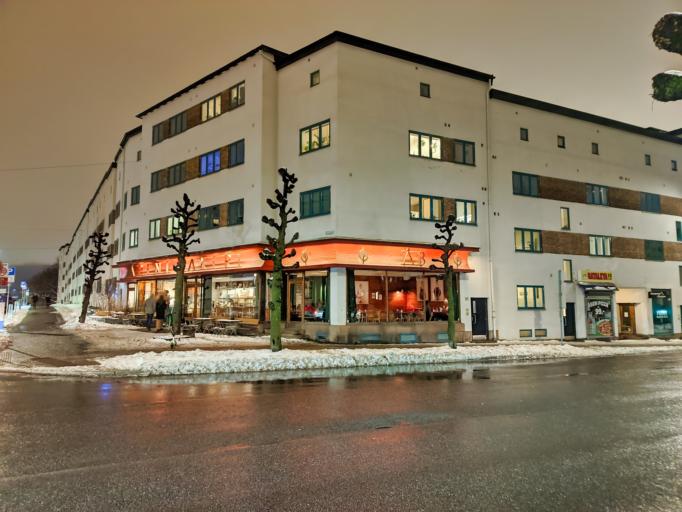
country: NO
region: Oslo
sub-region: Oslo
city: Oslo
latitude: 59.9395
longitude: 10.7742
